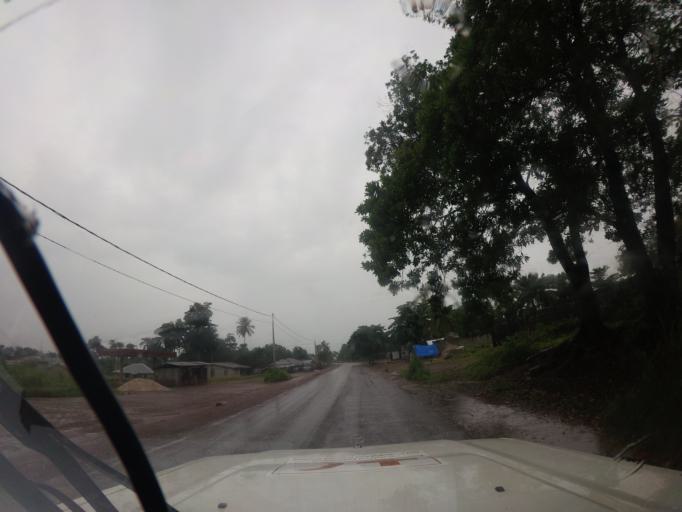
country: SL
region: Northern Province
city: Makeni
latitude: 8.9108
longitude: -12.0318
